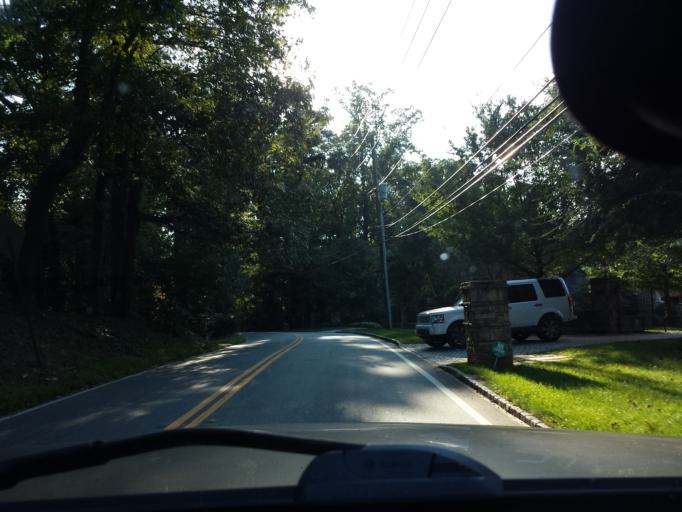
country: US
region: Georgia
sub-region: Cobb County
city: Vinings
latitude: 33.8767
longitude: -84.4130
